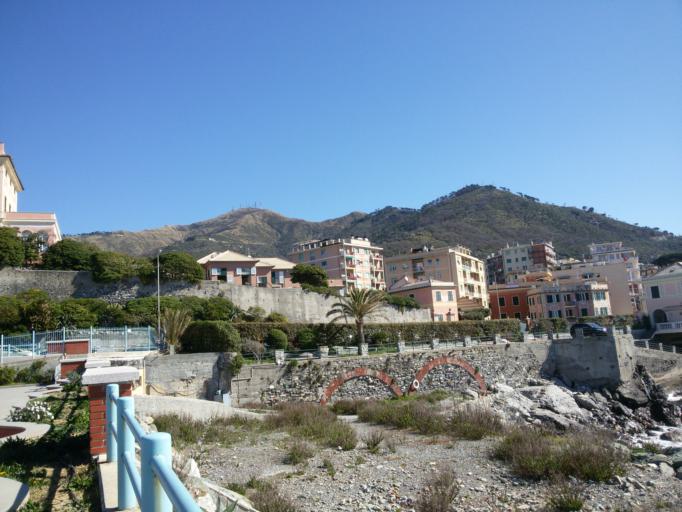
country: IT
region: Liguria
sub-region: Provincia di Genova
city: Bogliasco
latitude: 44.3851
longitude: 9.0093
